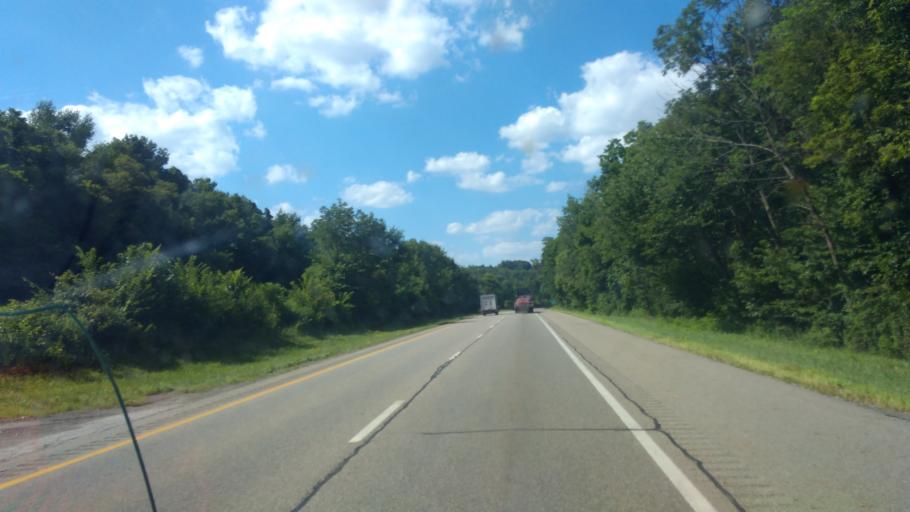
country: US
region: Ohio
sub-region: Stark County
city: Richville
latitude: 40.7210
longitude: -81.4209
